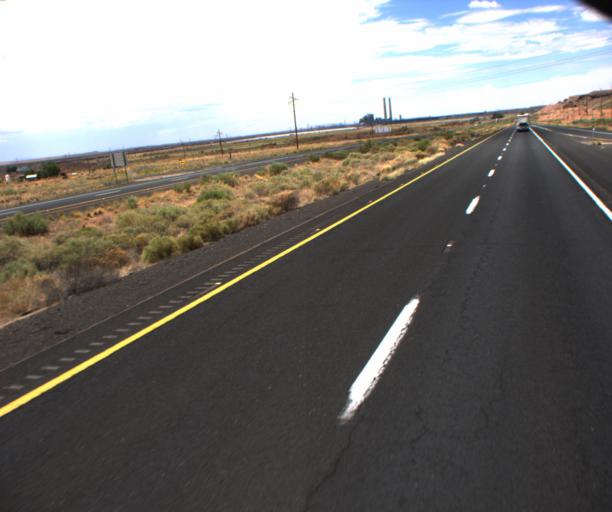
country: US
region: Arizona
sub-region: Navajo County
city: Joseph City
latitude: 34.9237
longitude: -110.2614
